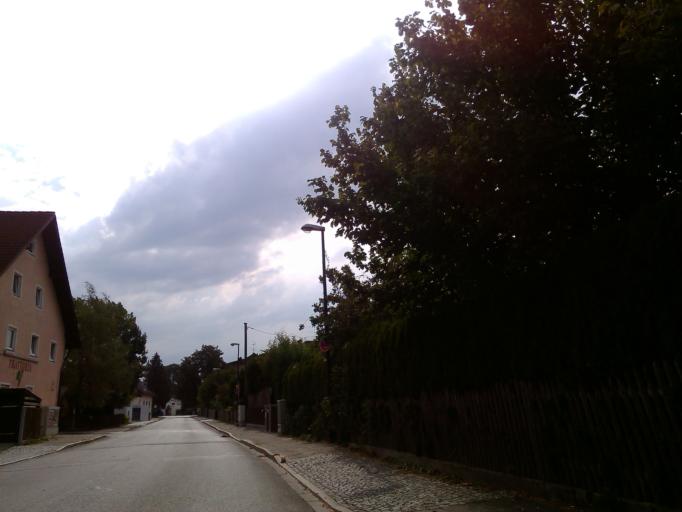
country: DE
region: Bavaria
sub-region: Upper Bavaria
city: Puchheim
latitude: 48.1361
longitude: 11.3548
